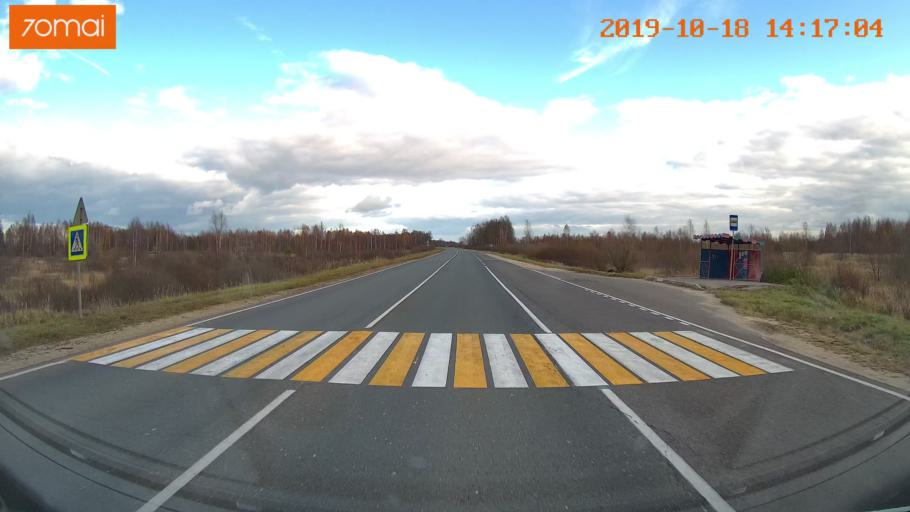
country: RU
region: Rjazan
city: Spas-Klepiki
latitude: 55.1403
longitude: 40.3608
